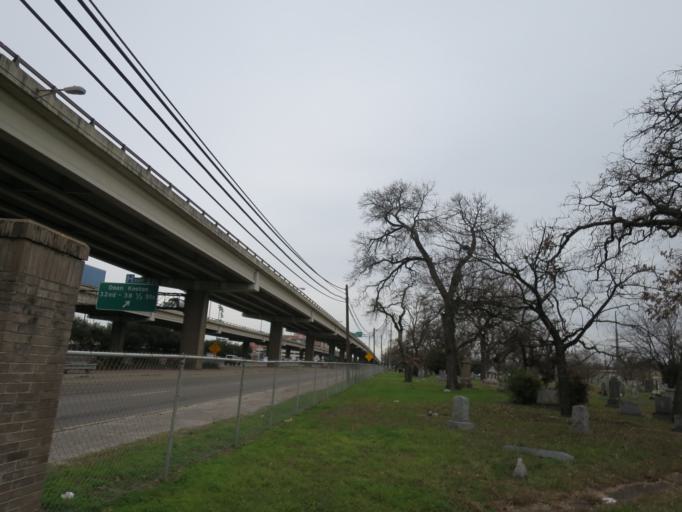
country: US
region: Texas
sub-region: Travis County
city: Austin
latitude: 30.2843
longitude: -97.7261
